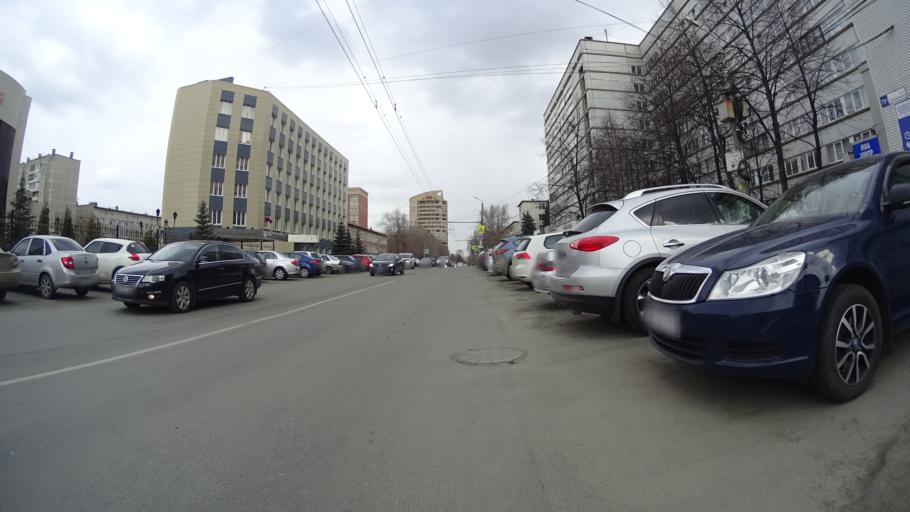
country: RU
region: Chelyabinsk
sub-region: Gorod Chelyabinsk
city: Chelyabinsk
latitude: 55.1573
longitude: 61.3712
